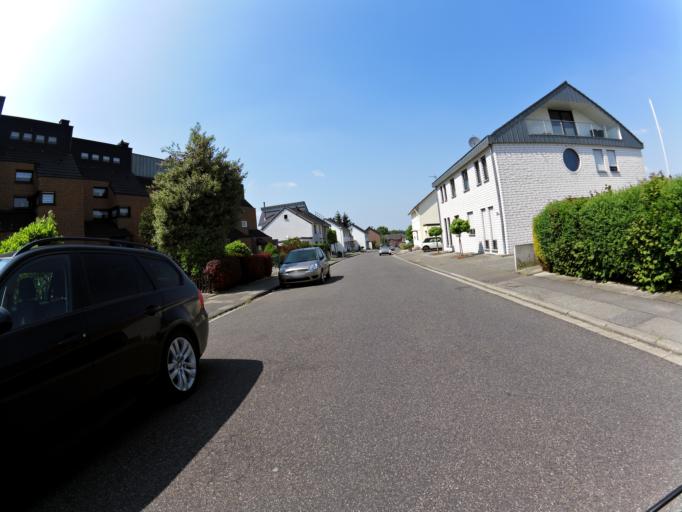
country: DE
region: North Rhine-Westphalia
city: Siersdorf
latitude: 50.8995
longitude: 6.2332
